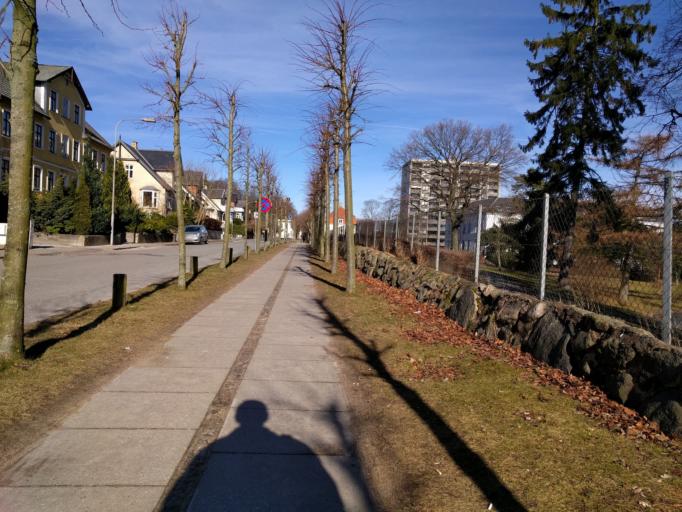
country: DK
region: Capital Region
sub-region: Helsingor Kommune
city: Helsingor
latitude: 56.0395
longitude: 12.6050
